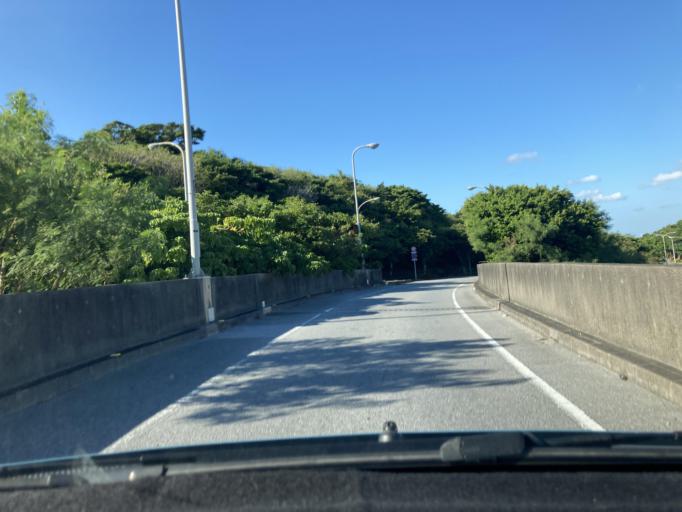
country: JP
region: Okinawa
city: Ginowan
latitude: 26.2566
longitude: 127.7281
